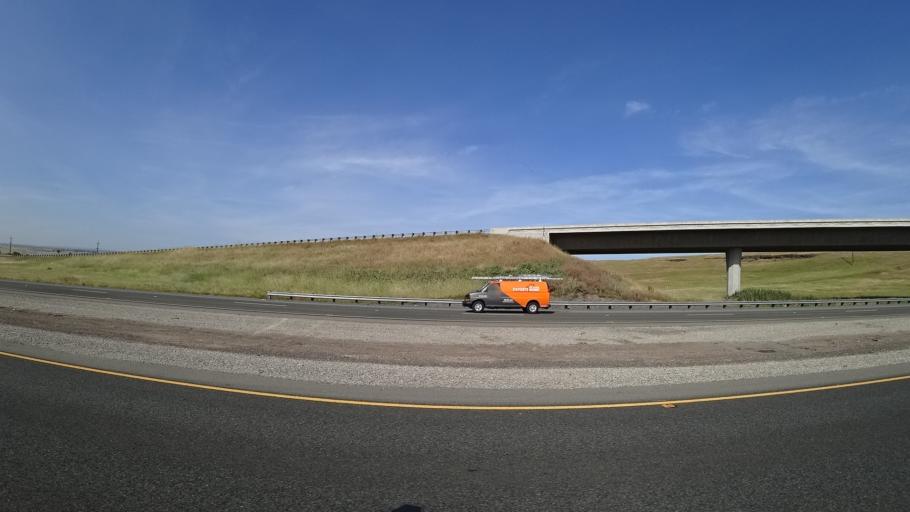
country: US
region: California
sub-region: Butte County
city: Durham
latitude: 39.6232
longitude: -121.6948
